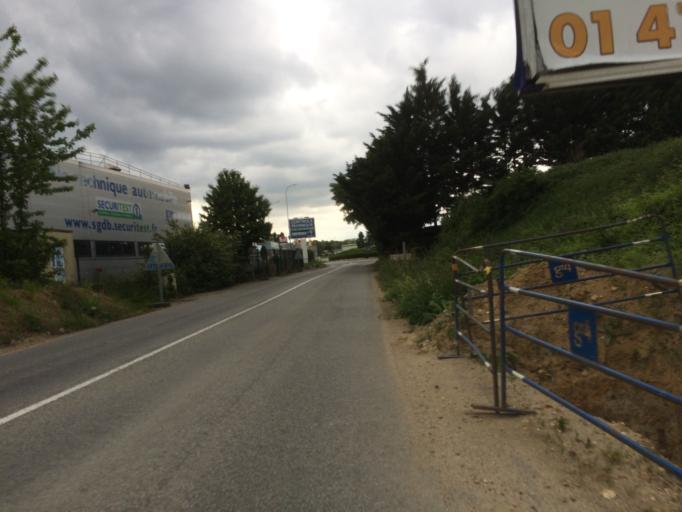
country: FR
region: Ile-de-France
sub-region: Departement de l'Essonne
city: Le Plessis-Pate
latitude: 48.6204
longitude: 2.3415
